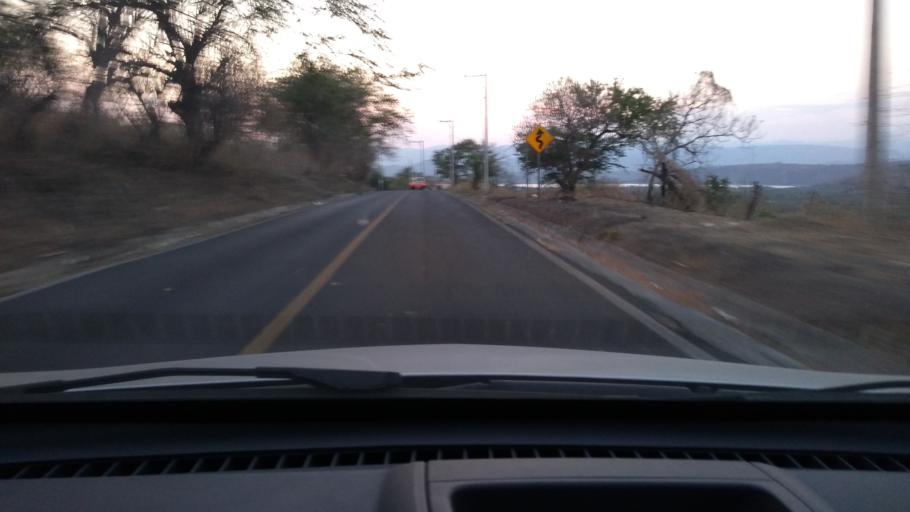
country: MX
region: Morelos
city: Coatetelco
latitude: 18.7219
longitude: -99.3104
